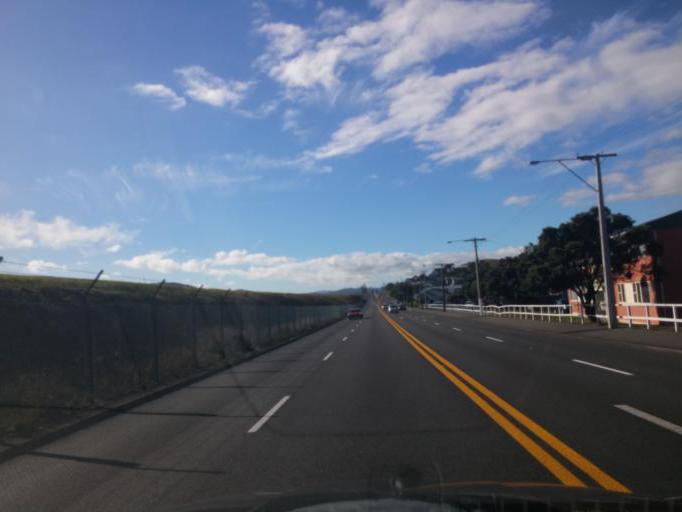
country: NZ
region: Wellington
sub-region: Wellington City
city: Wellington
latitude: -41.3239
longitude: 174.8089
